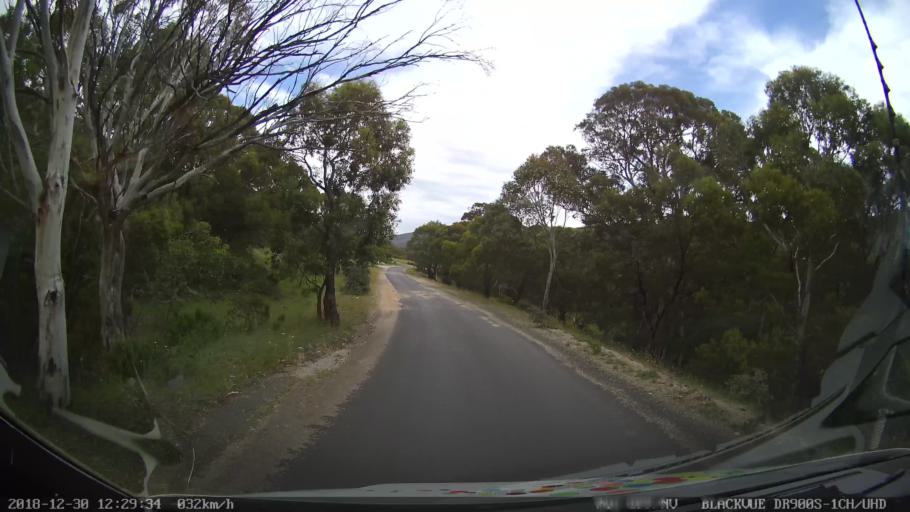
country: AU
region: New South Wales
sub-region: Snowy River
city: Jindabyne
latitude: -36.3232
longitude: 148.4771
